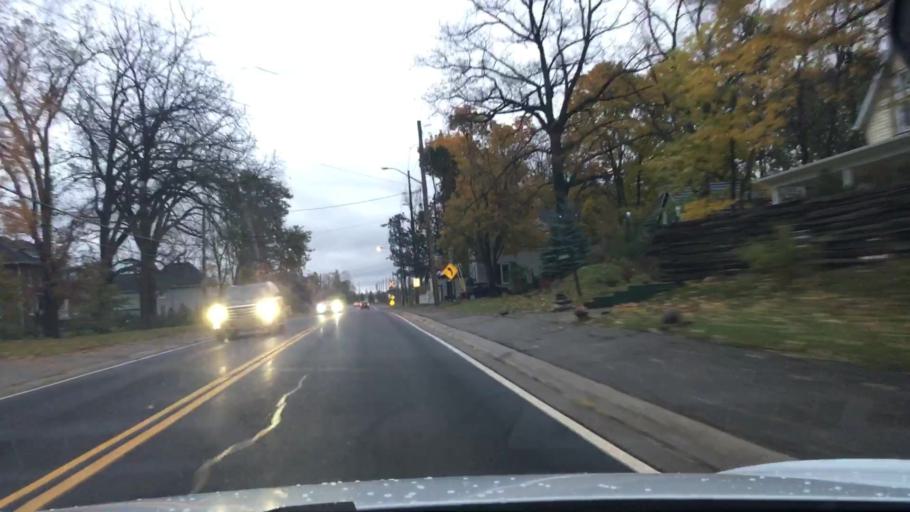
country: CA
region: Ontario
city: Pickering
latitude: 43.8867
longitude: -79.1998
